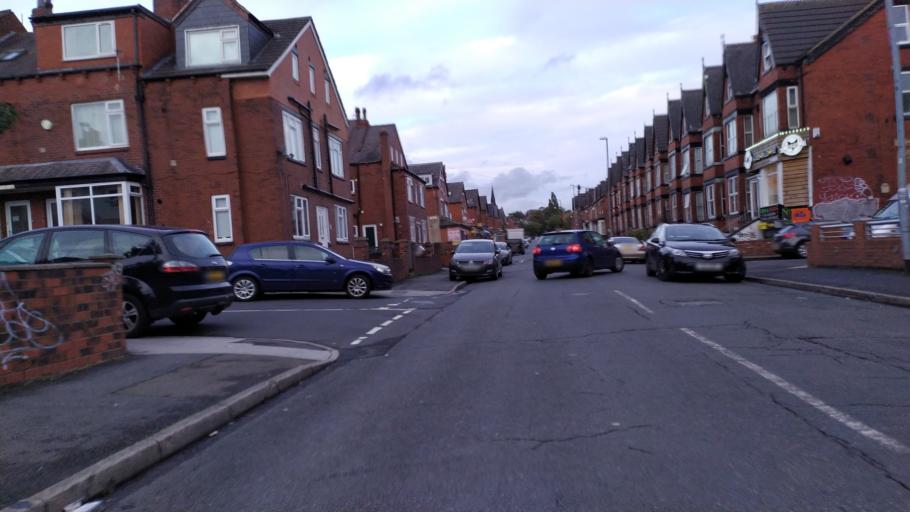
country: GB
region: England
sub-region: City and Borough of Leeds
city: Leeds
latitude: 53.8115
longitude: -1.5722
